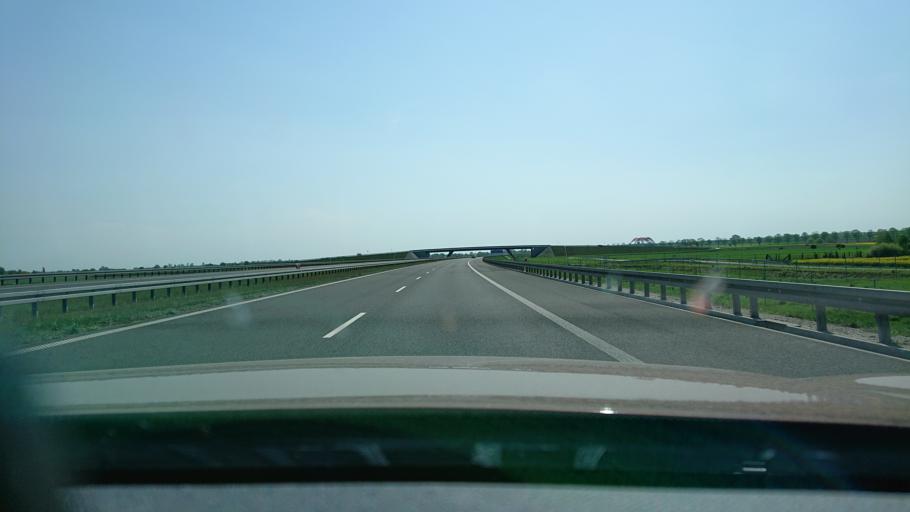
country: PL
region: Subcarpathian Voivodeship
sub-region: Powiat przeworski
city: Rozborz
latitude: 50.0742
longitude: 22.5444
